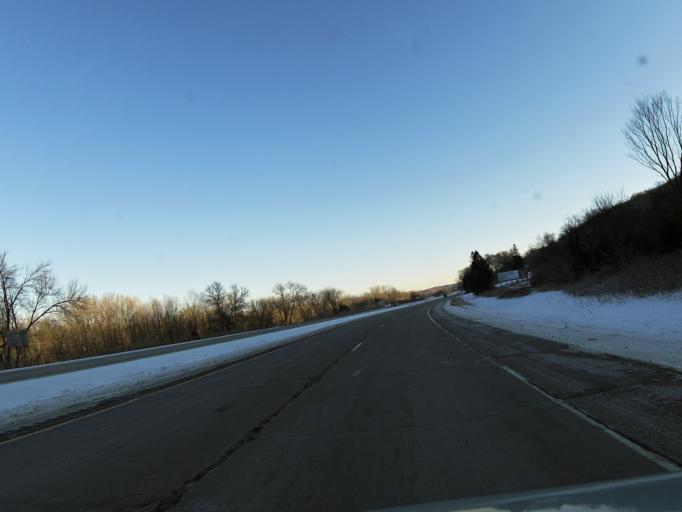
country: US
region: Minnesota
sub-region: Scott County
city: Jordan
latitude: 44.6802
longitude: -93.6198
